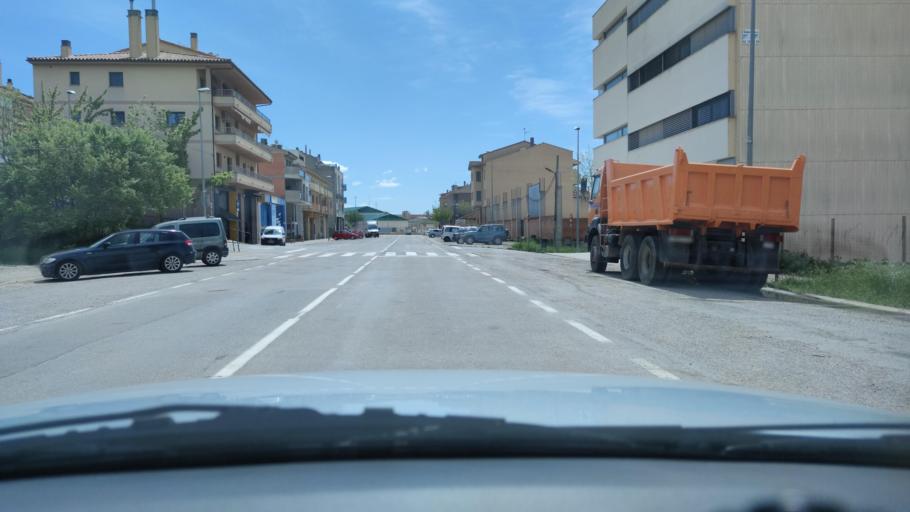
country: ES
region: Catalonia
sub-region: Provincia de Lleida
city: Solsona
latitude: 41.9998
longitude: 1.5194
